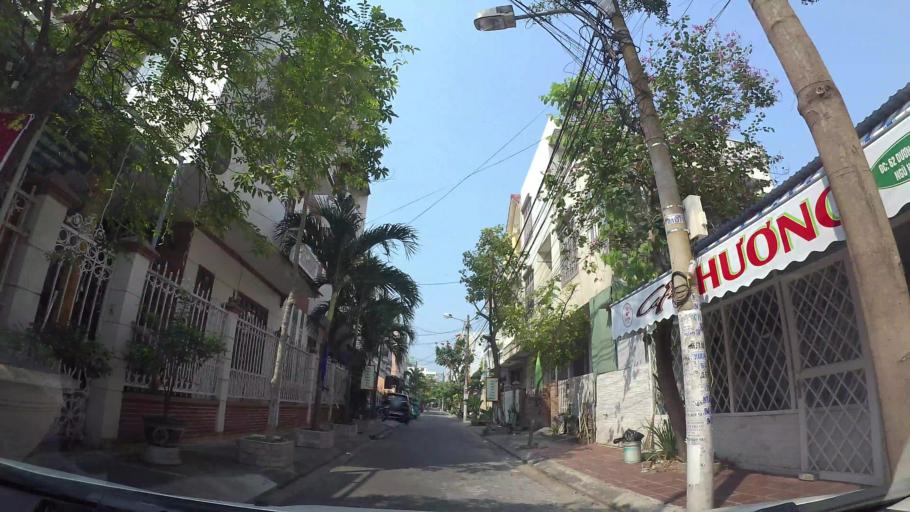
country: VN
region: Da Nang
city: Son Tra
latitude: 16.0415
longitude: 108.2438
